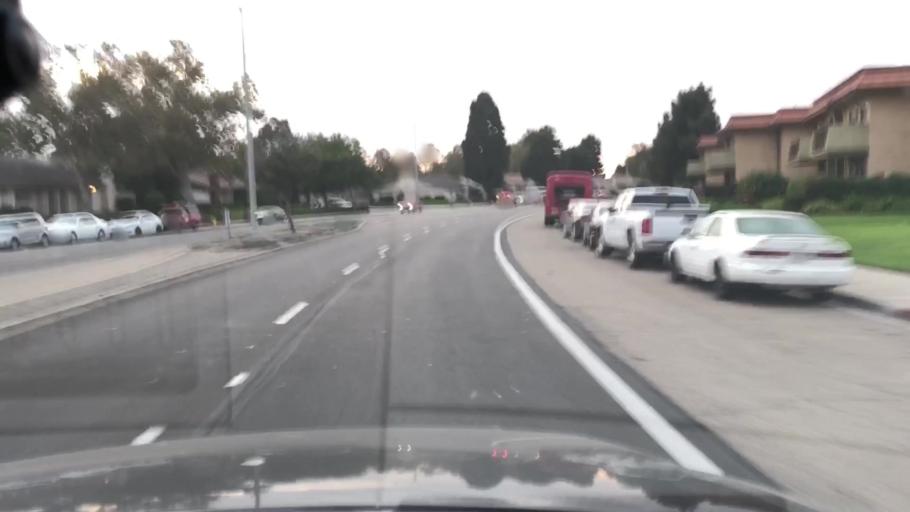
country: US
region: California
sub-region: Ventura County
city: El Rio
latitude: 34.2263
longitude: -119.1799
